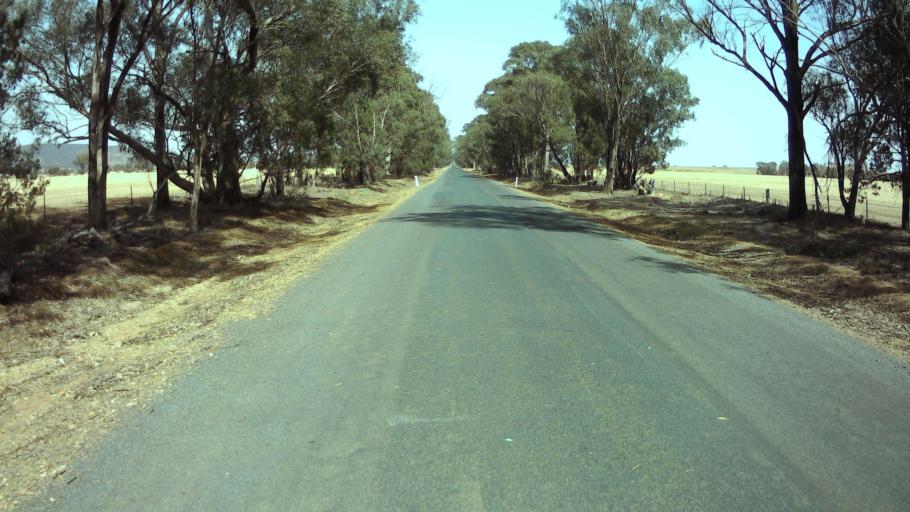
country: AU
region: New South Wales
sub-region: Weddin
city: Grenfell
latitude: -33.8646
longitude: 148.0416
